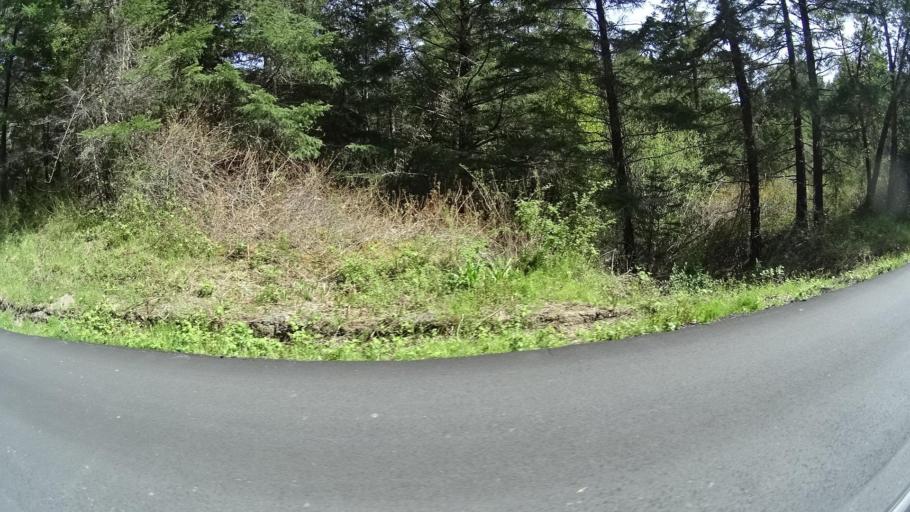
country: US
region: California
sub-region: Humboldt County
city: Redway
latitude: 40.4359
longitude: -123.7717
